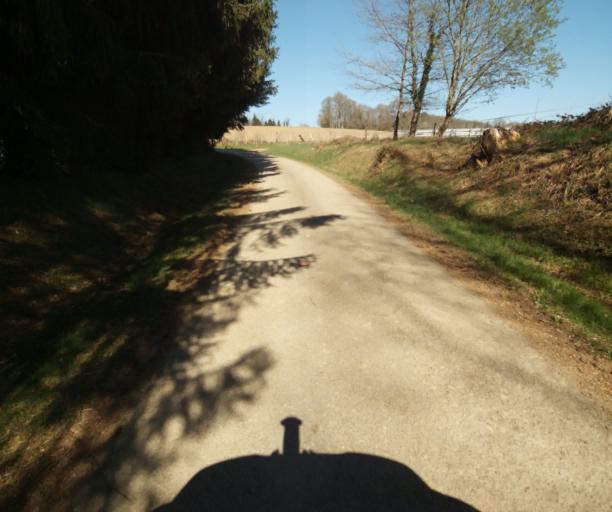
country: FR
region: Limousin
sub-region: Departement de la Correze
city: Saint-Mexant
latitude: 45.3214
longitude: 1.6054
